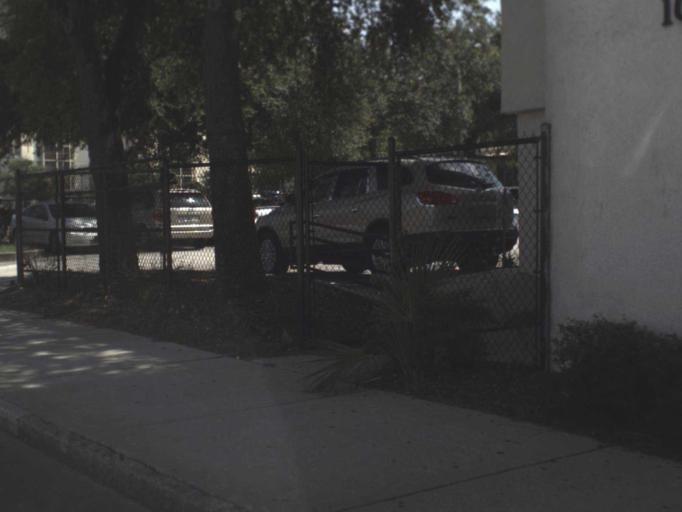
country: US
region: Florida
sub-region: Hillsborough County
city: Tampa
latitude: 27.9601
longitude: -82.4595
